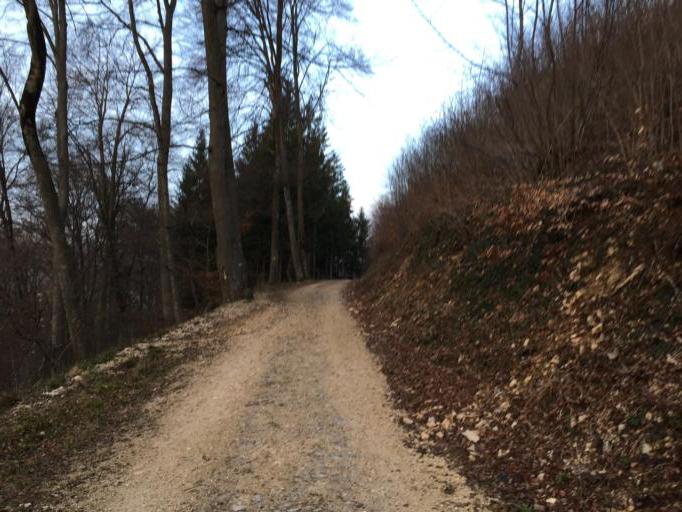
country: CH
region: Basel-Landschaft
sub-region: Bezirk Sissach
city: Sissach
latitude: 47.4579
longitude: 7.8145
